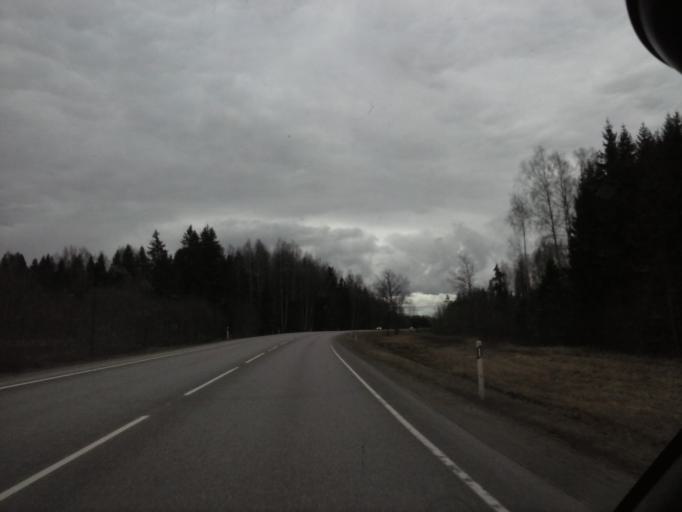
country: EE
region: Jaervamaa
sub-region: Paide linn
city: Paide
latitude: 58.8159
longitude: 25.7570
